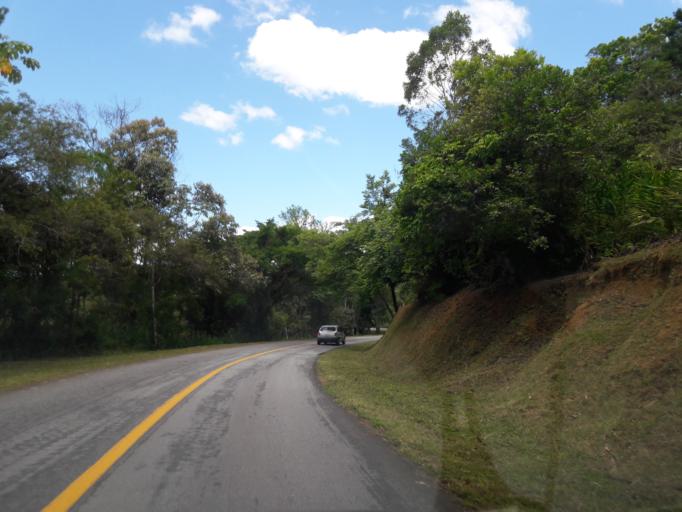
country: BR
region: Parana
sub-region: Antonina
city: Antonina
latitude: -25.4344
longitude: -48.7951
